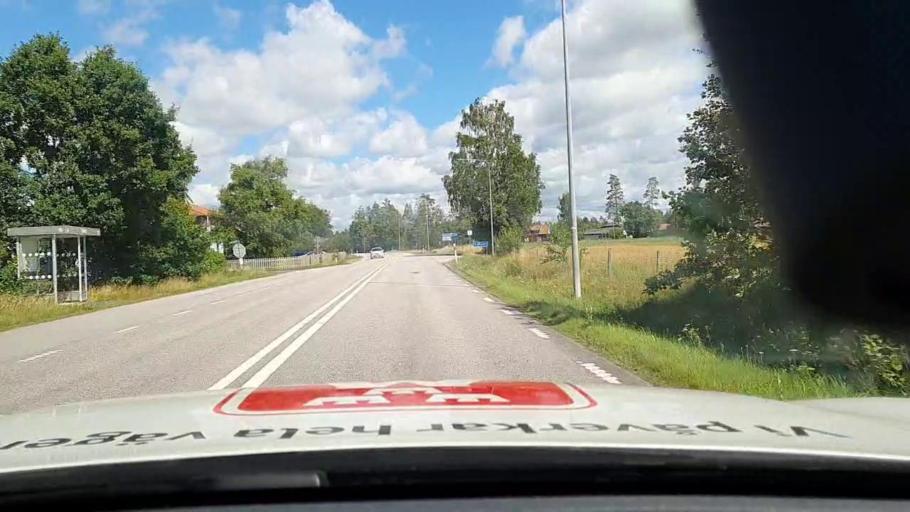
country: SE
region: Vaestra Goetaland
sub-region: Skovde Kommun
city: Stopen
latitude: 58.4353
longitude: 13.9290
